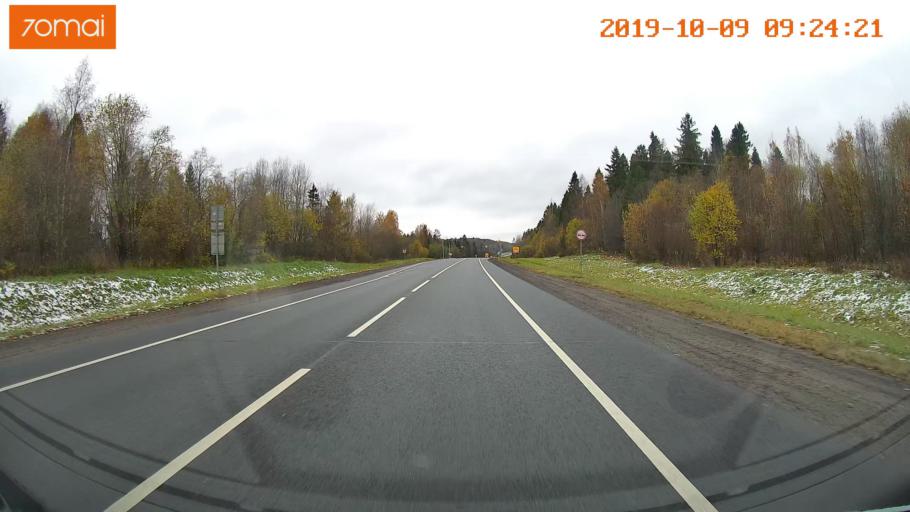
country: RU
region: Vologda
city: Vologda
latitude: 59.0778
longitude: 40.0177
